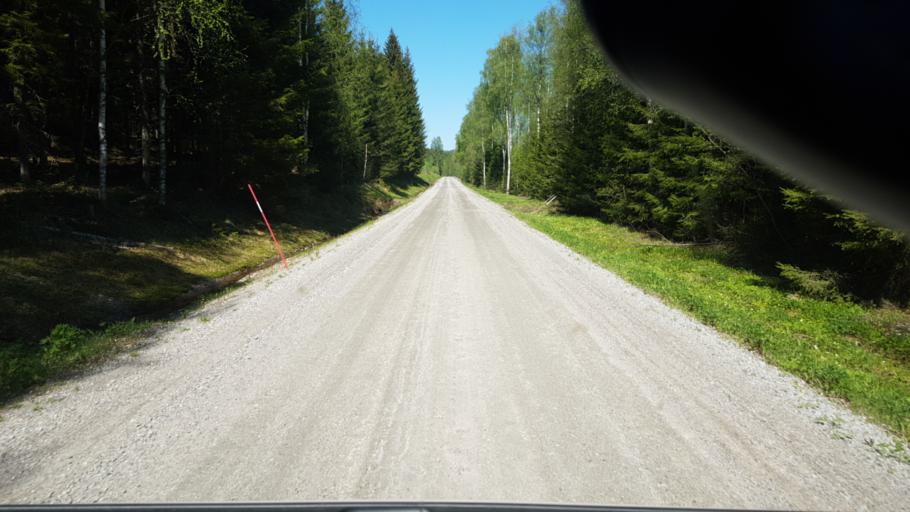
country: SE
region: Vaermland
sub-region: Arvika Kommun
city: Arvika
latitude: 59.8063
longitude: 12.7479
